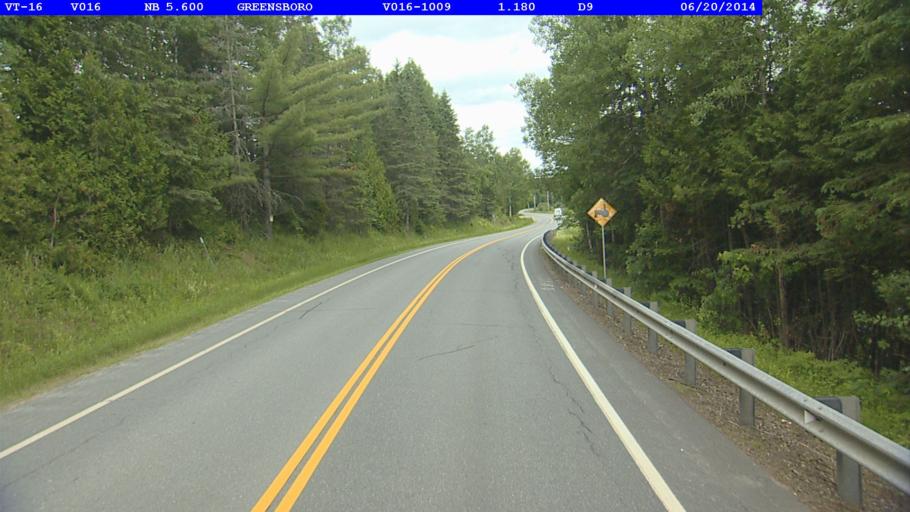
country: US
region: Vermont
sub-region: Caledonia County
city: Hardwick
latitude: 44.5596
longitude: -72.2579
